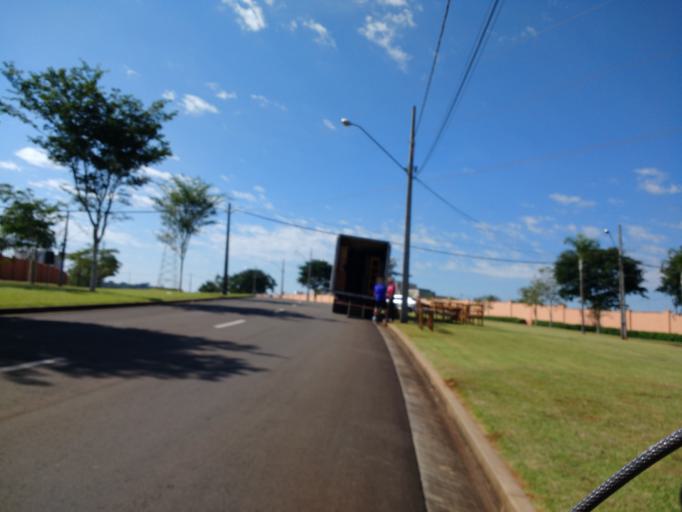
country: BR
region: Parana
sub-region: Londrina
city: Londrina
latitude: -23.3532
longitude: -51.1879
